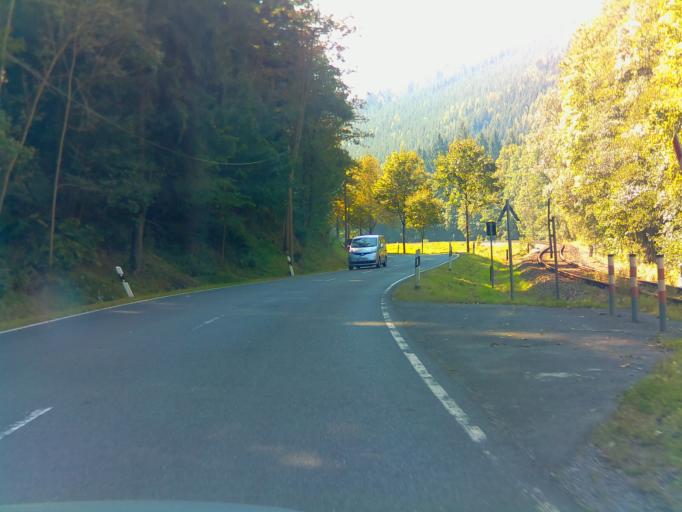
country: DE
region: Thuringia
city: Leutenberg
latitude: 50.5474
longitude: 11.4690
